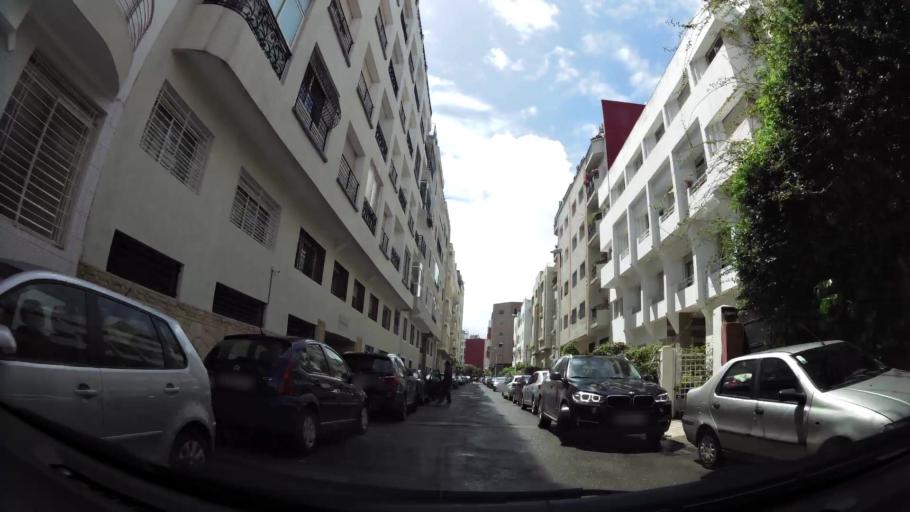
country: MA
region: Grand Casablanca
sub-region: Casablanca
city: Casablanca
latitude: 33.5755
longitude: -7.6378
